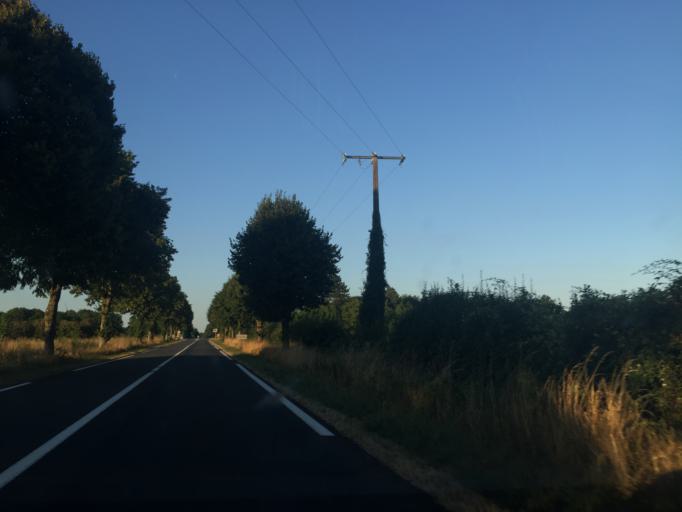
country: FR
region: Poitou-Charentes
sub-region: Departement de la Vienne
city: Rouille
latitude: 46.4021
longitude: 0.0748
